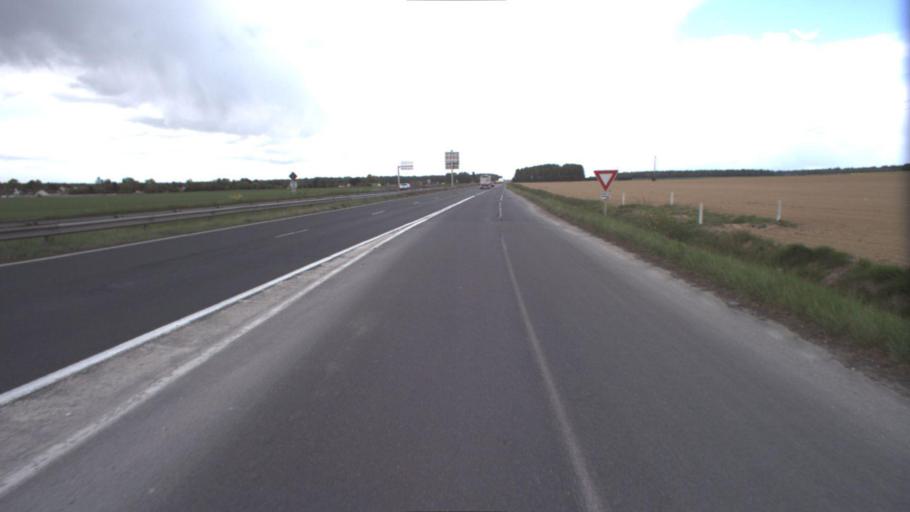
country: FR
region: Ile-de-France
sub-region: Departement de Seine-et-Marne
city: Rozay-en-Brie
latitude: 48.6855
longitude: 2.9349
